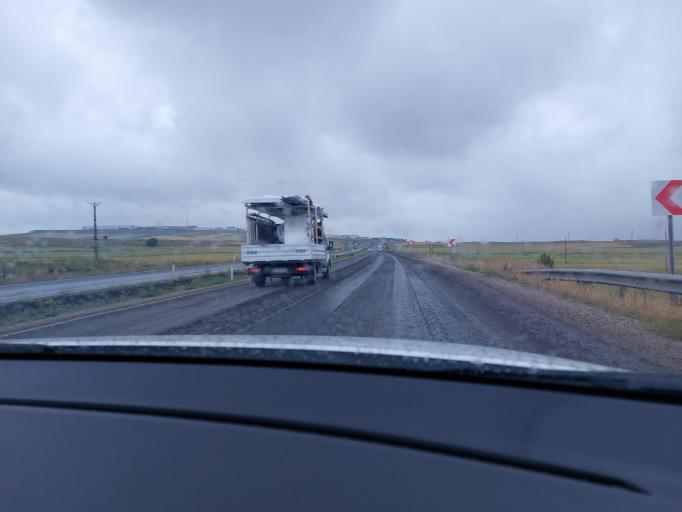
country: TR
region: Nevsehir
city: Dobada
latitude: 38.5389
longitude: 34.4526
